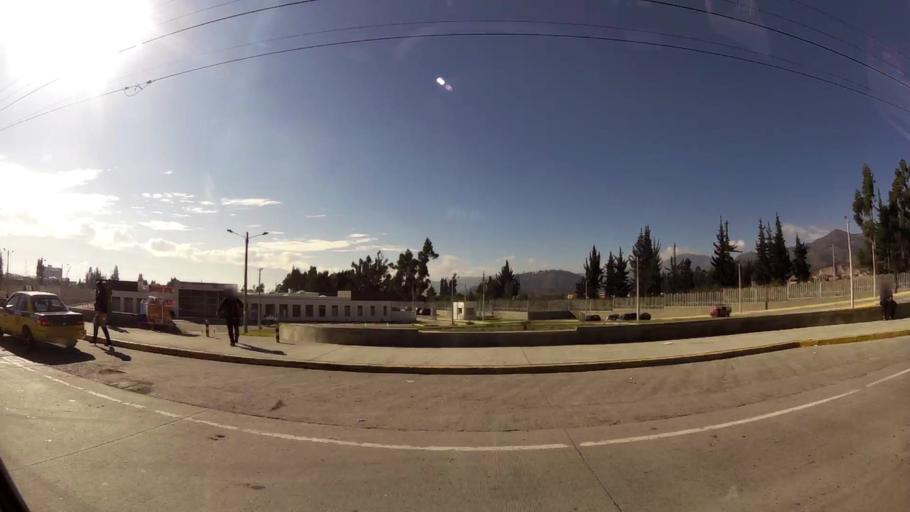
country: EC
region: Chimborazo
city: Riobamba
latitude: -1.6473
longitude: -78.6853
